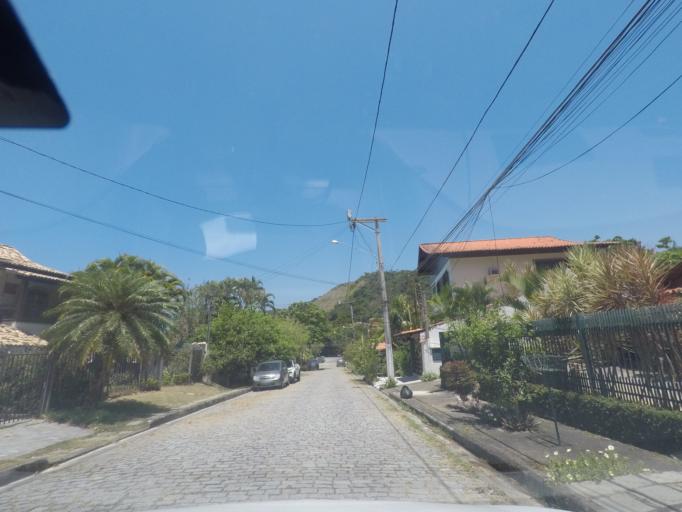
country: BR
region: Rio de Janeiro
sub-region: Niteroi
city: Niteroi
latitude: -22.9699
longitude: -43.0306
